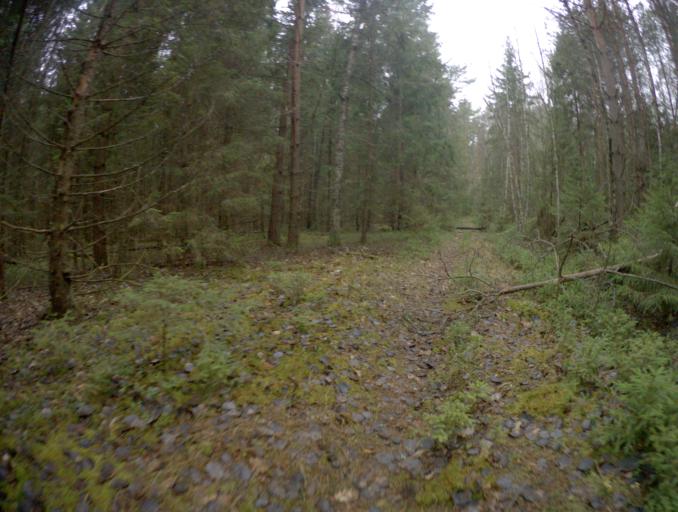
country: RU
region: Vladimir
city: Golovino
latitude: 56.0157
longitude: 40.5030
